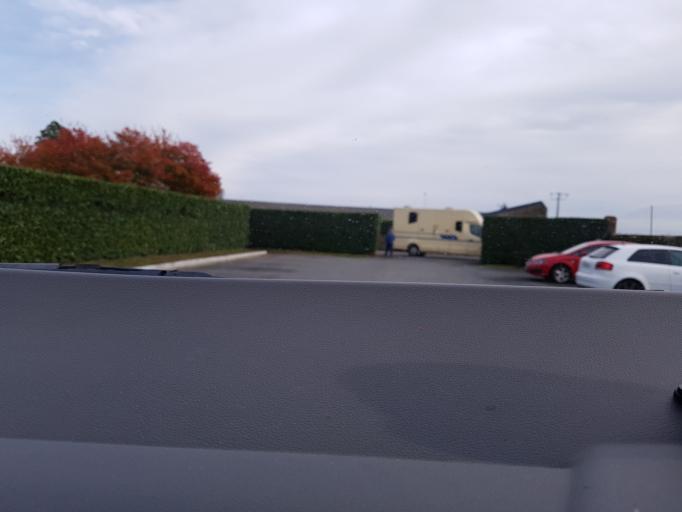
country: FR
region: Pays de la Loire
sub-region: Departement de Maine-et-Loire
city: Beaupreau
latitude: 47.1933
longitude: -0.9878
